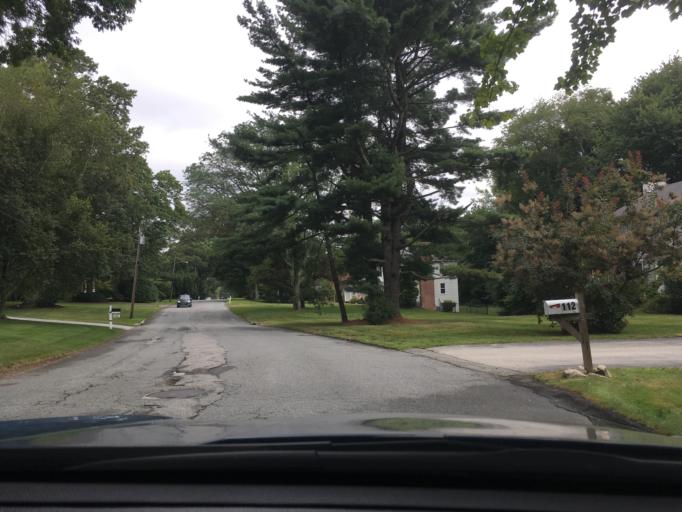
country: US
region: Rhode Island
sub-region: Kent County
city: East Greenwich
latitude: 41.6541
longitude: -71.4865
